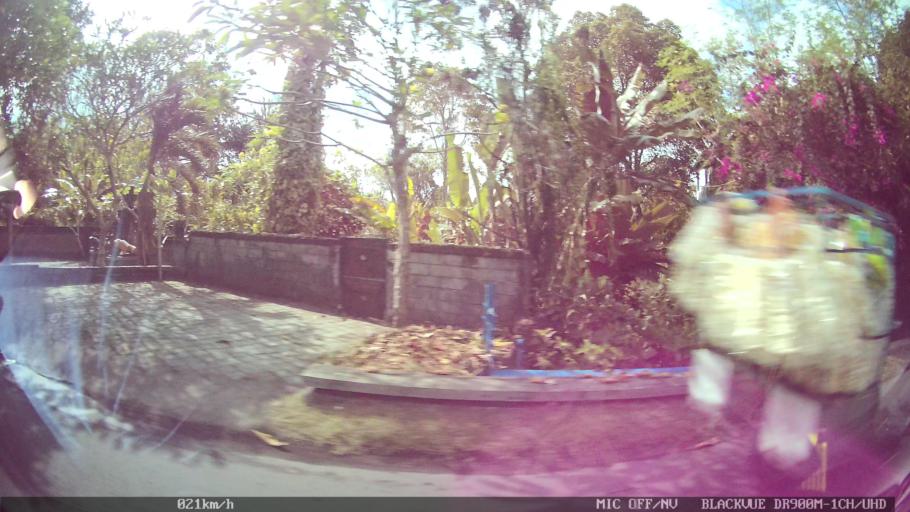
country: ID
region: Bali
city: Banjar Karangsuling
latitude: -8.6103
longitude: 115.2026
